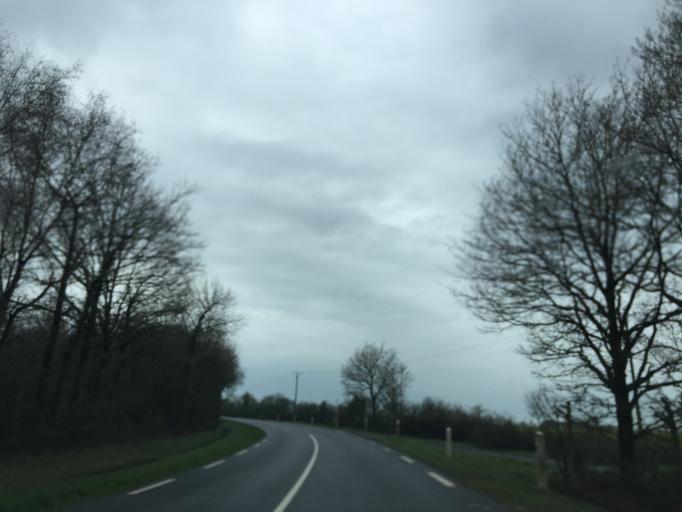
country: FR
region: Pays de la Loire
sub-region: Departement de la Loire-Atlantique
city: Moisdon-la-Riviere
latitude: 47.6553
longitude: -1.3800
